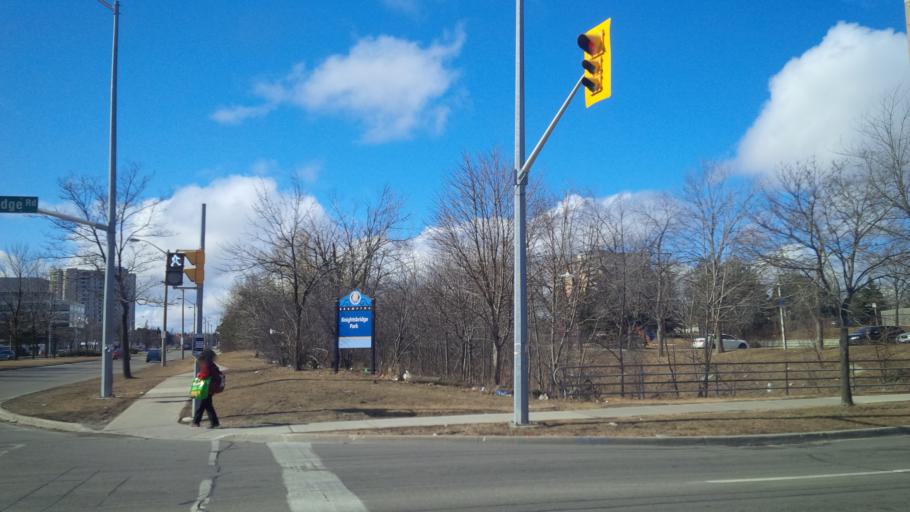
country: CA
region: Ontario
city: Brampton
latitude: 43.7183
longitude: -79.7172
